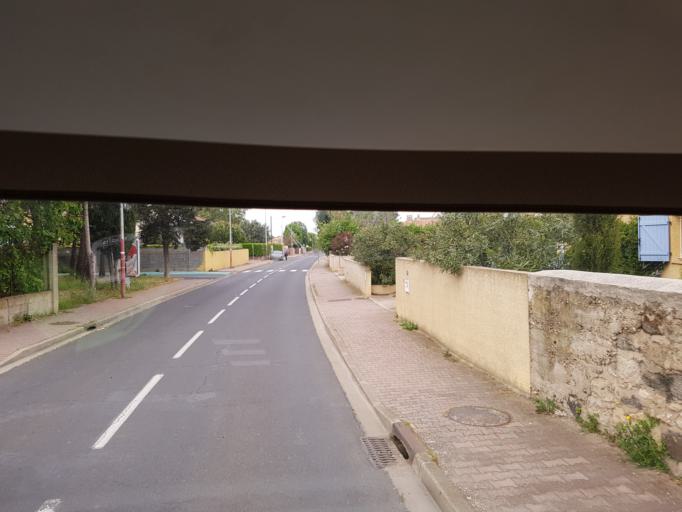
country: FR
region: Languedoc-Roussillon
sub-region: Departement de l'Herault
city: Serignan
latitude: 43.2787
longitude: 3.2738
